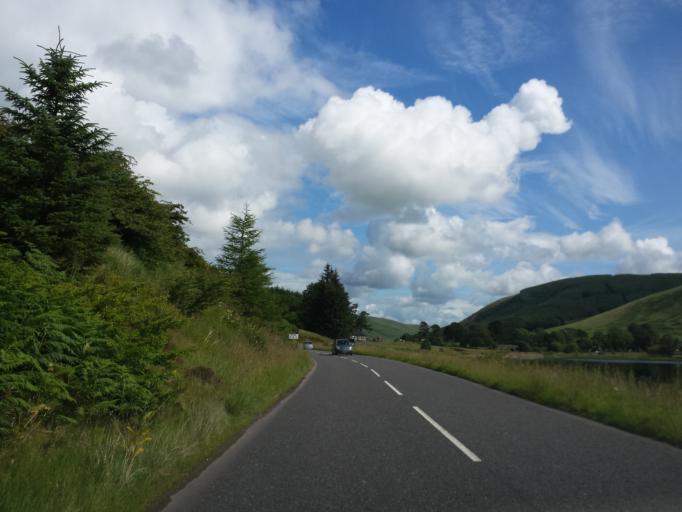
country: GB
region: Scotland
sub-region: The Scottish Borders
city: Peebles
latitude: 55.4691
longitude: -3.2089
